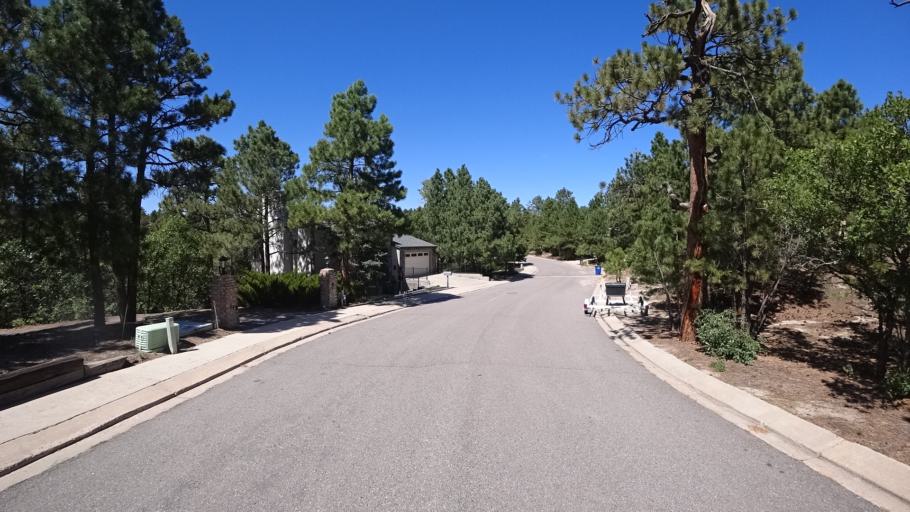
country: US
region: Colorado
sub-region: El Paso County
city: Colorado Springs
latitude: 38.9191
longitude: -104.7978
